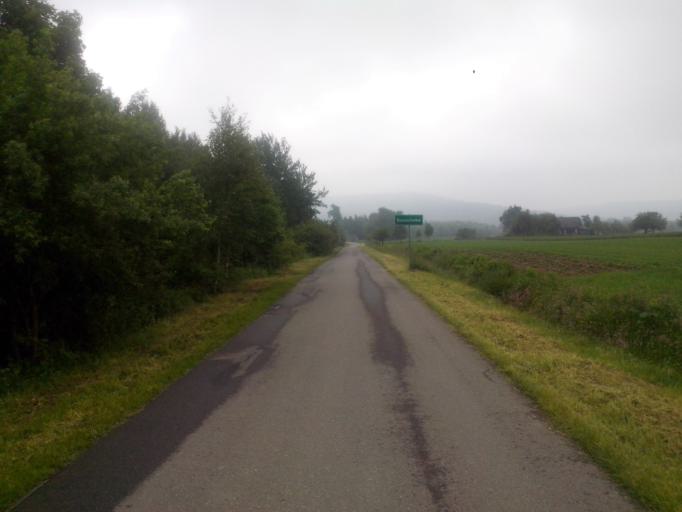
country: PL
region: Subcarpathian Voivodeship
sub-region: Powiat strzyzowski
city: Wysoka Strzyzowska
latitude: 49.8099
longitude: 21.7822
